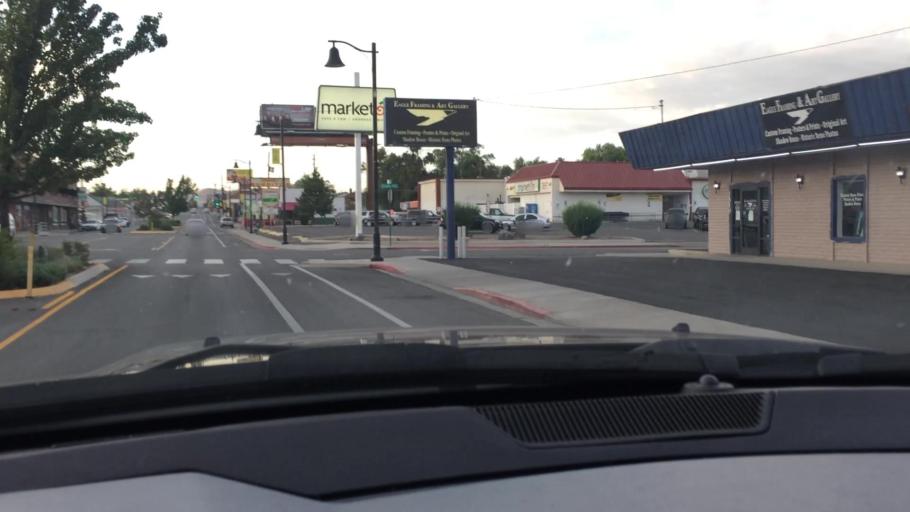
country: US
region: Nevada
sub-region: Washoe County
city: Reno
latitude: 39.5102
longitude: -119.8031
